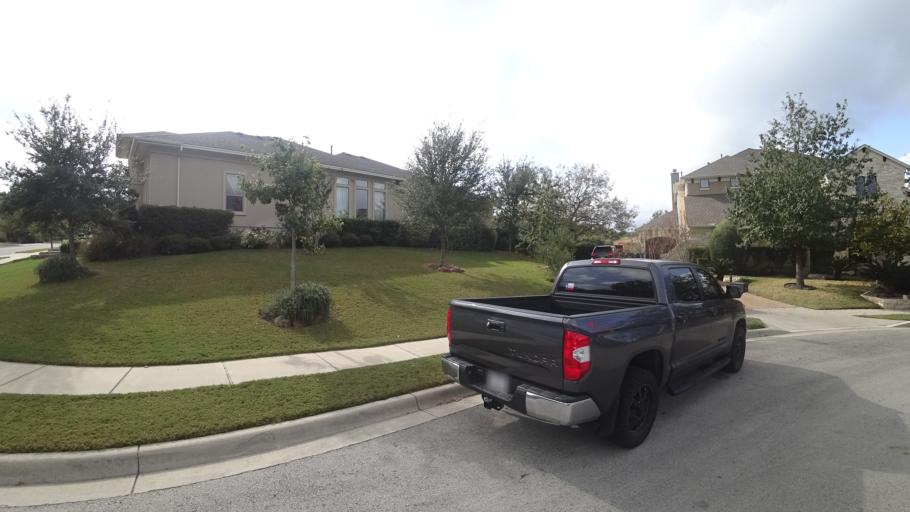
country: US
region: Texas
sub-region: Travis County
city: Barton Creek
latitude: 30.3161
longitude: -97.9010
